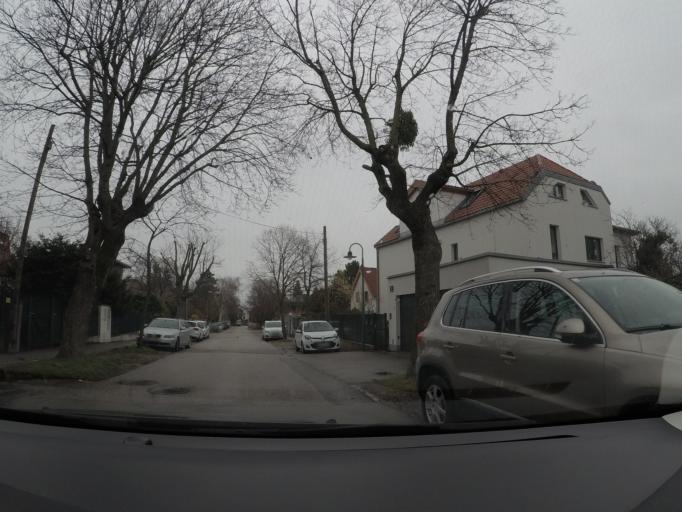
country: AT
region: Lower Austria
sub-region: Politischer Bezirk Modling
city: Perchtoldsdorf
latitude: 48.1293
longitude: 16.2724
